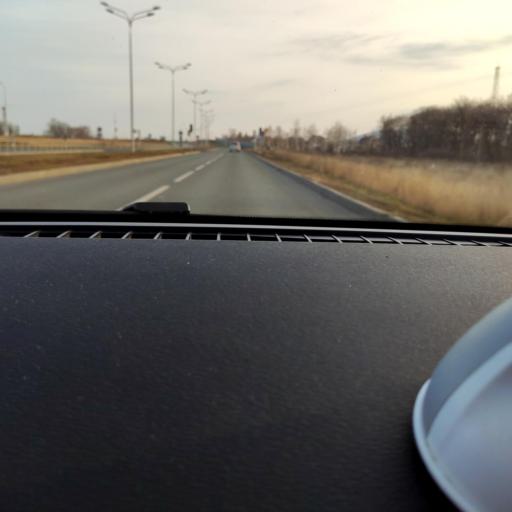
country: RU
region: Samara
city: Samara
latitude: 53.2877
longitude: 50.2321
